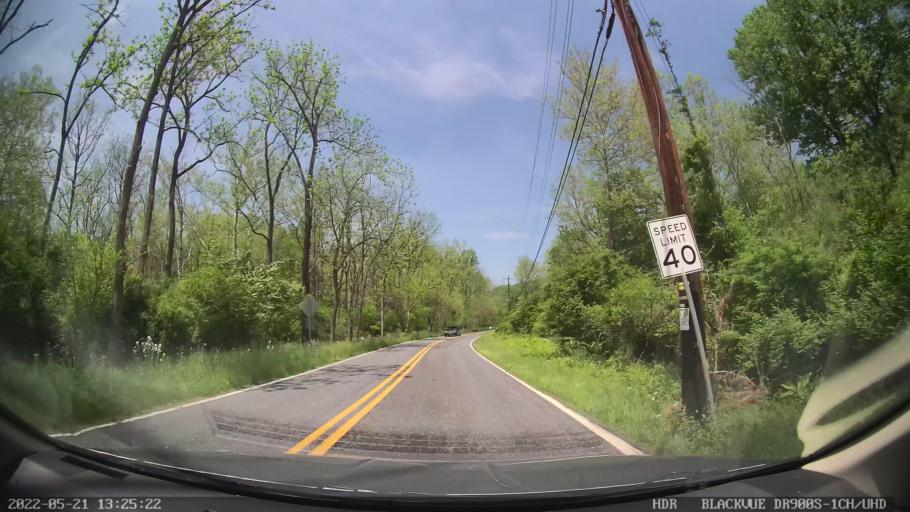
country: US
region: Pennsylvania
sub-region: Berks County
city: Bally
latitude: 40.3998
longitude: -75.6115
